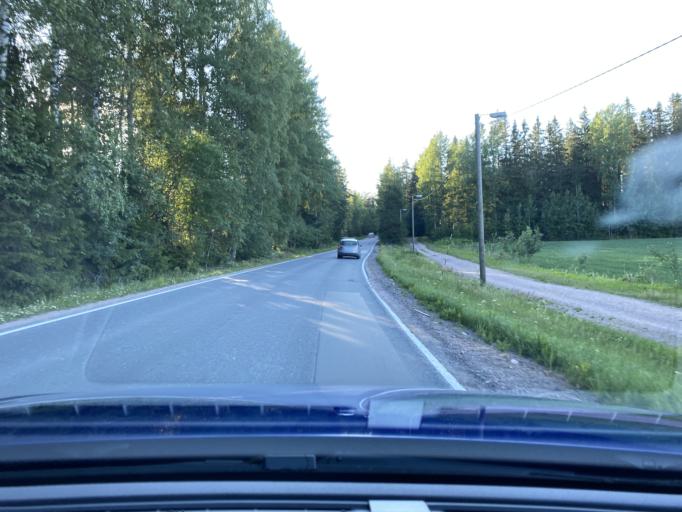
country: FI
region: Haeme
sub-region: Riihimaeki
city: Riihimaeki
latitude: 60.7255
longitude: 24.6978
